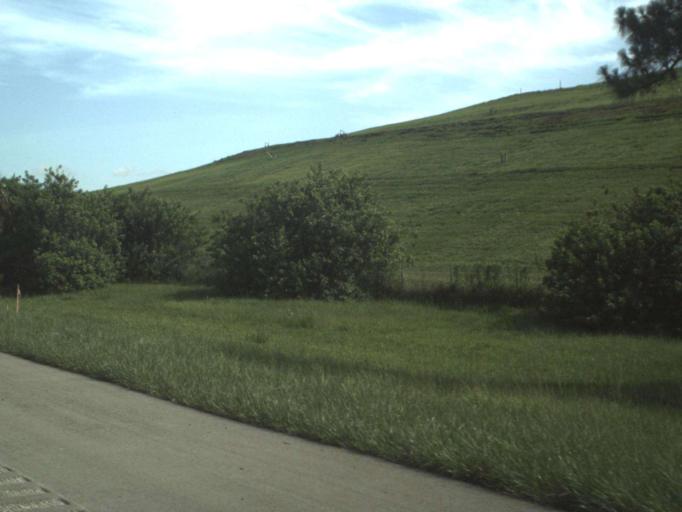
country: US
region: Florida
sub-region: Indian River County
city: West Vero Corridor
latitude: 27.5775
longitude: -80.4945
